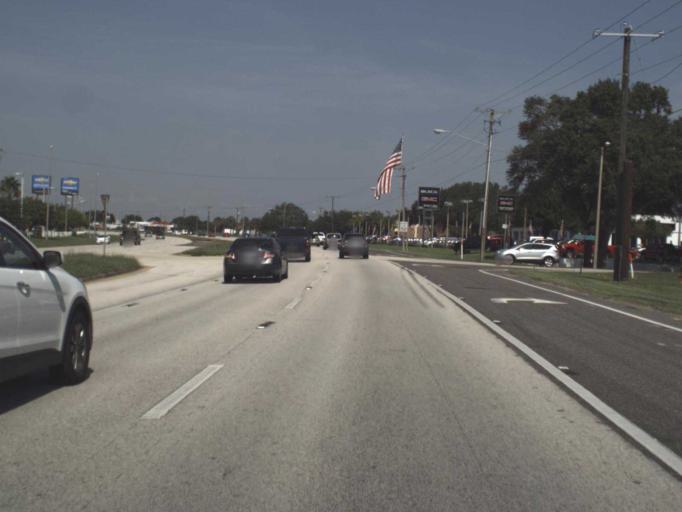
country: US
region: Florida
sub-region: Hillsborough County
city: Palm River-Clair Mel
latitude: 27.9487
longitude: -82.3440
